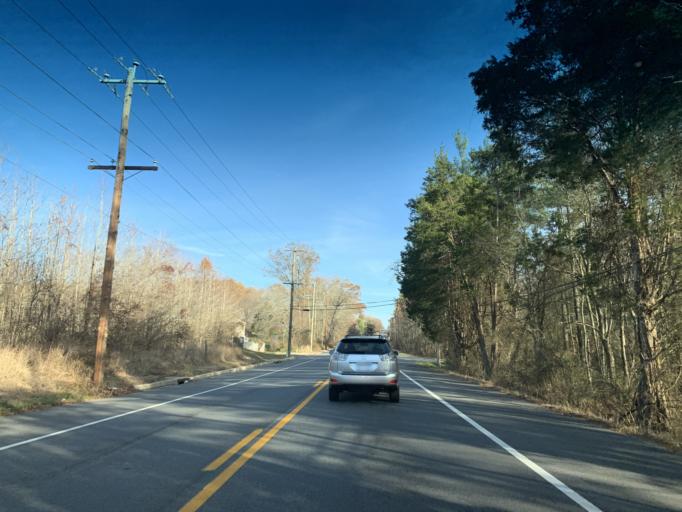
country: US
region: Maryland
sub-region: Cecil County
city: North East
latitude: 39.6019
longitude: -75.9314
